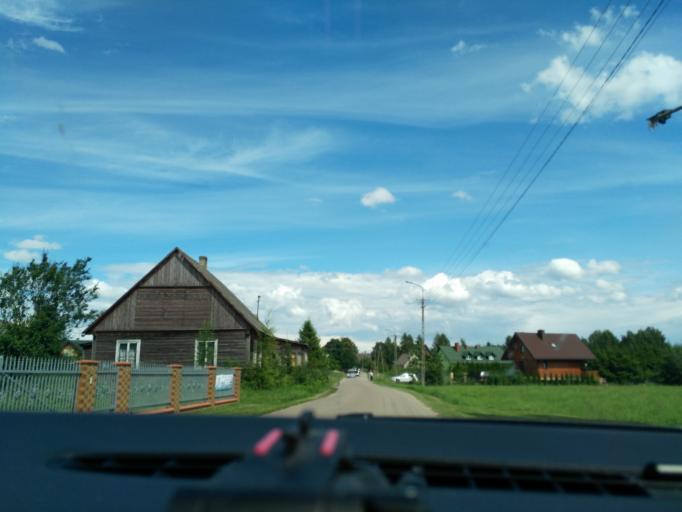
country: PL
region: Podlasie
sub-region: Powiat sejnenski
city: Sejny
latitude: 54.0382
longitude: 23.3386
